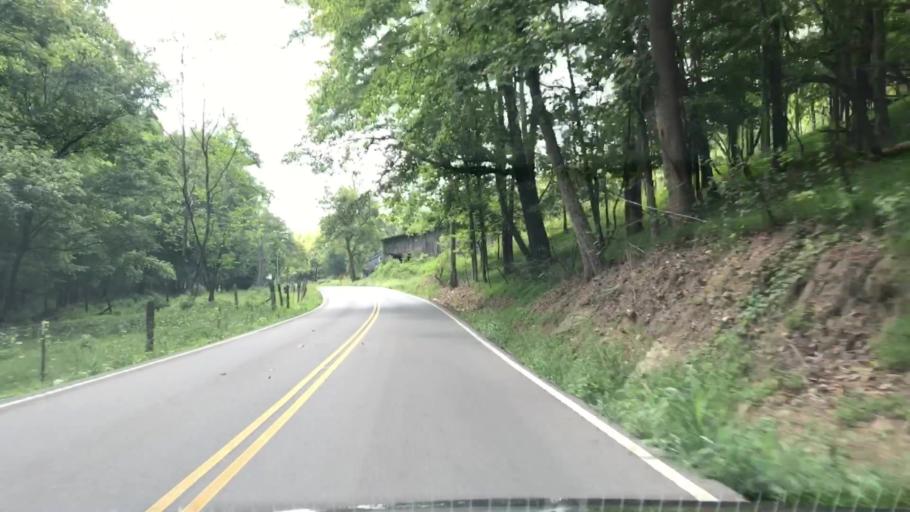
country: US
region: Tennessee
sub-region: Sumner County
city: Westmoreland
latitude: 36.4900
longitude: -86.1913
